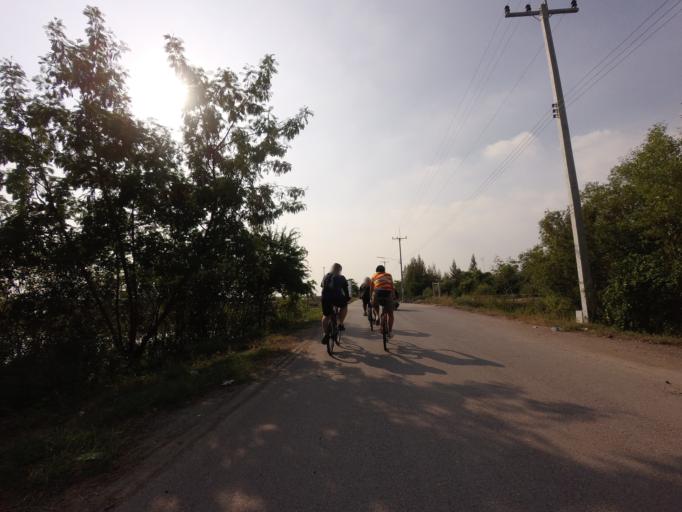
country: TH
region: Samut Sakhon
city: Samut Sakhon
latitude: 13.4988
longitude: 100.3567
